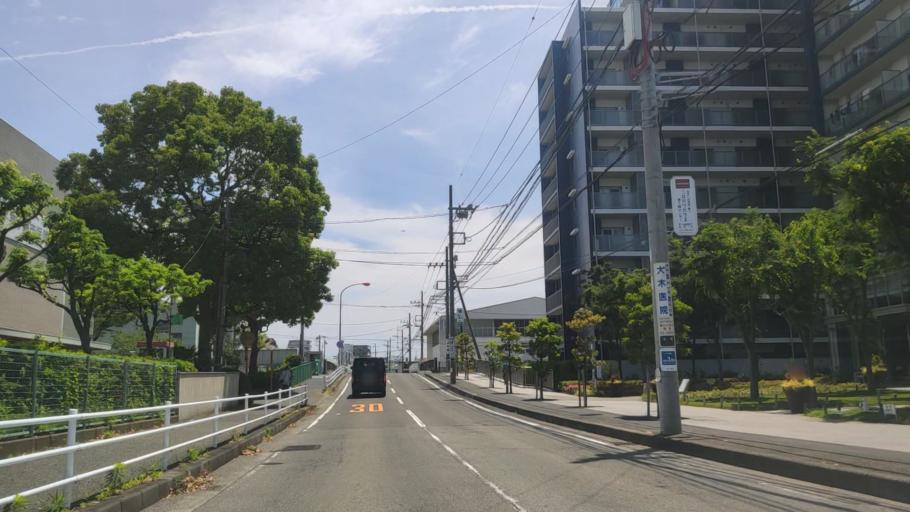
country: JP
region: Kanagawa
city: Chigasaki
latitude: 35.3342
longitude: 139.3994
